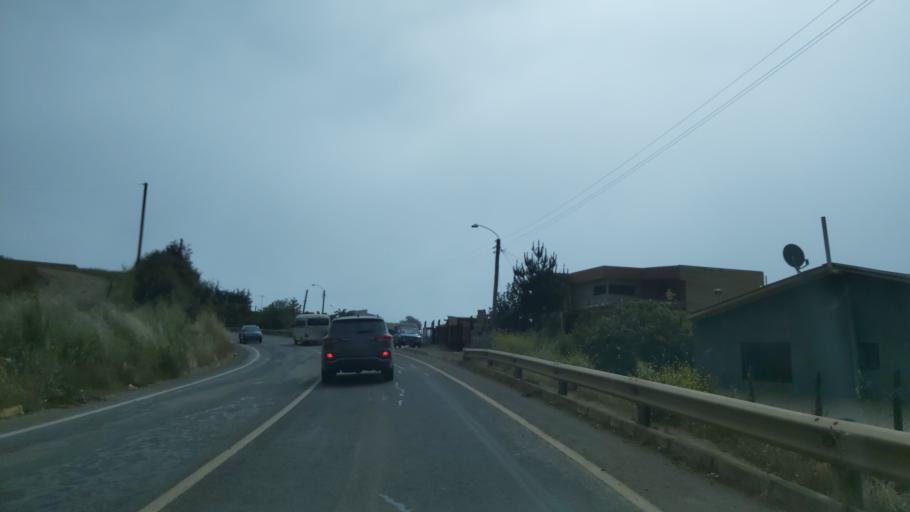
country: CL
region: Maule
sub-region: Provincia de Cauquenes
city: Cauquenes
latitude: -35.8743
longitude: -72.6653
